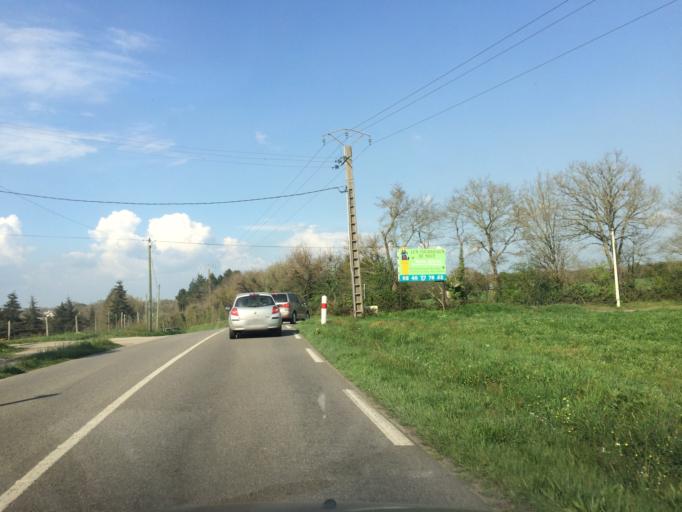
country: FR
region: Pays de la Loire
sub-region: Departement de la Loire-Atlantique
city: Suce-sur-Erdre
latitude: 47.3255
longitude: -1.5119
